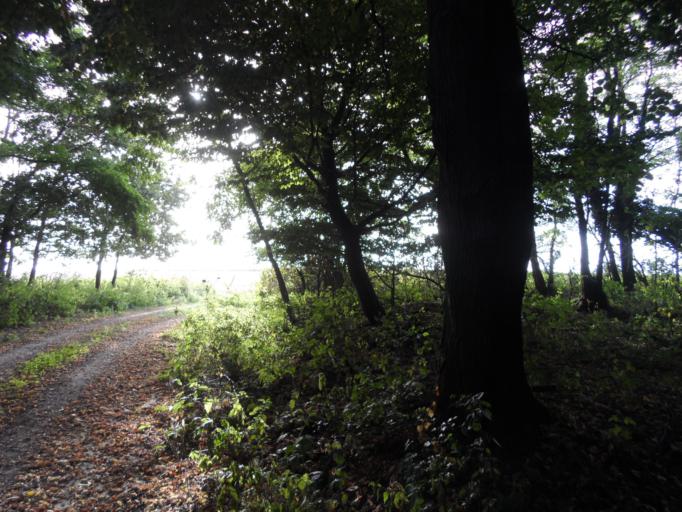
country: HU
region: Veszprem
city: Urkut
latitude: 47.1785
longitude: 17.6272
